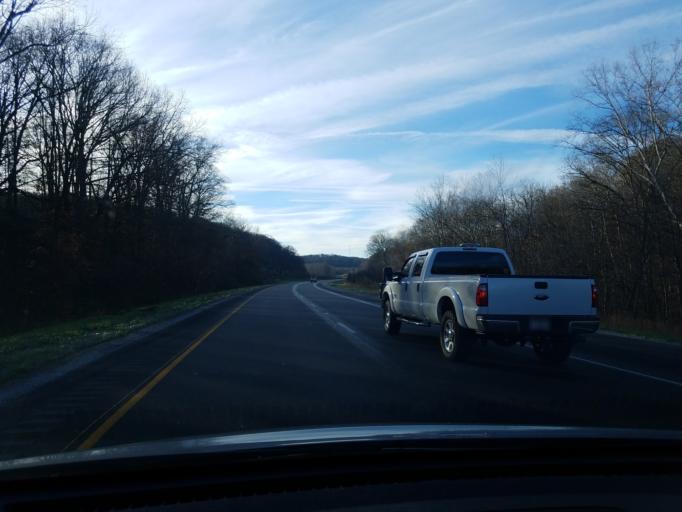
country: US
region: Indiana
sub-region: Crawford County
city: English
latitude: 38.2370
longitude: -86.3883
